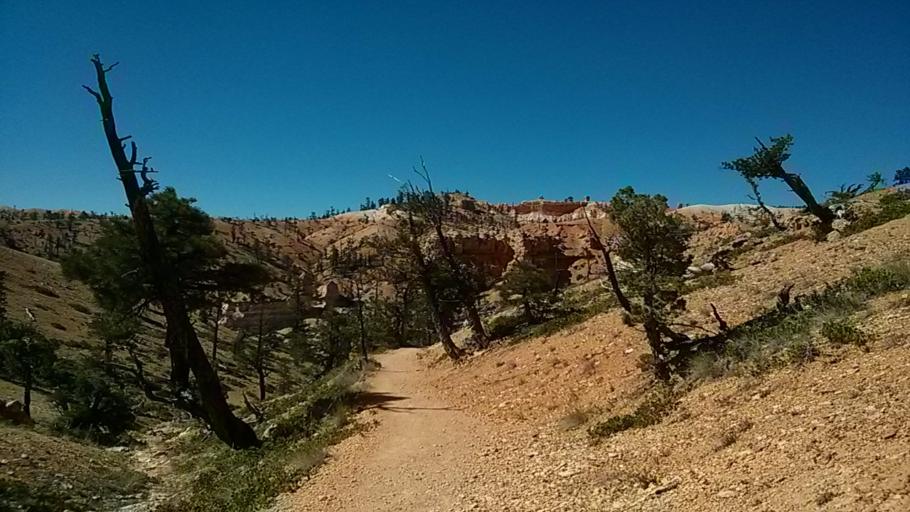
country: US
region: Utah
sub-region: Garfield County
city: Panguitch
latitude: 37.6346
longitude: -112.1448
